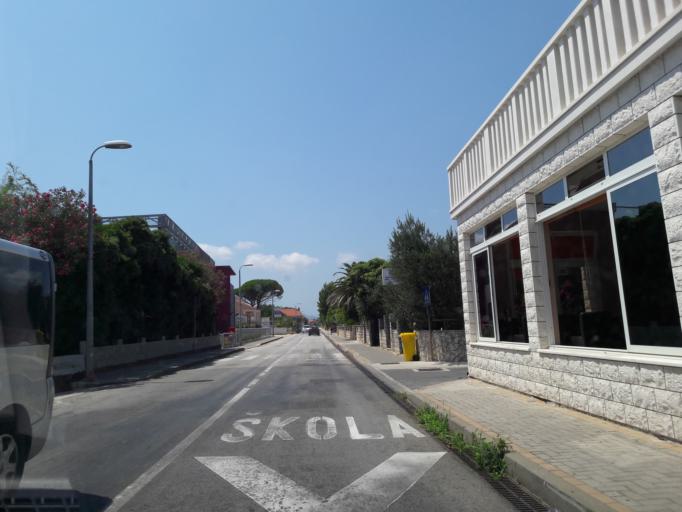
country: HR
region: Dubrovacko-Neretvanska
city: Orebic
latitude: 42.9759
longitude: 17.1821
